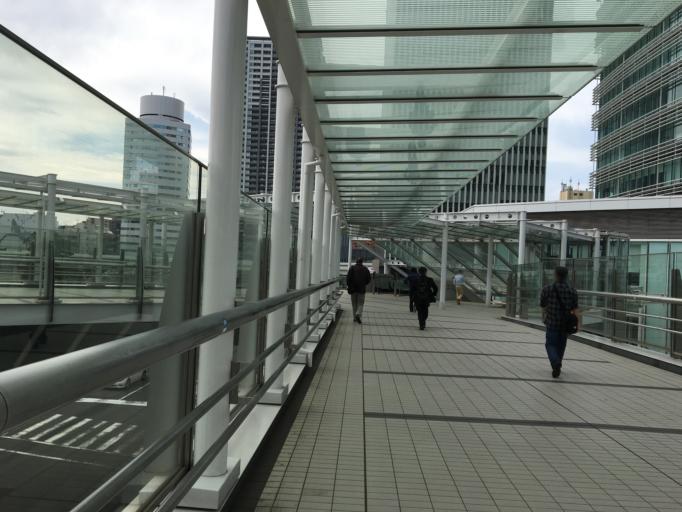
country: JP
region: Kanagawa
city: Yokohama
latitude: 35.4629
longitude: 139.6270
